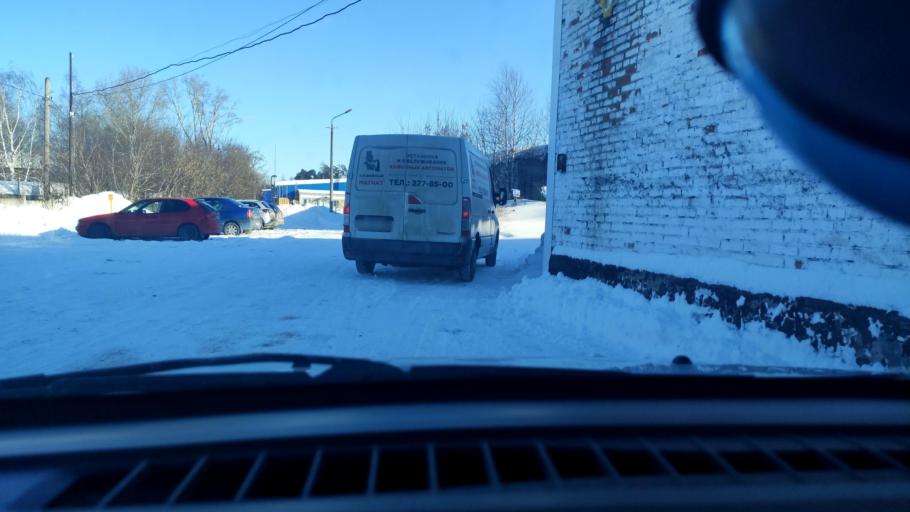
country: RU
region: Perm
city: Overyata
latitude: 57.9969
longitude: 55.9165
